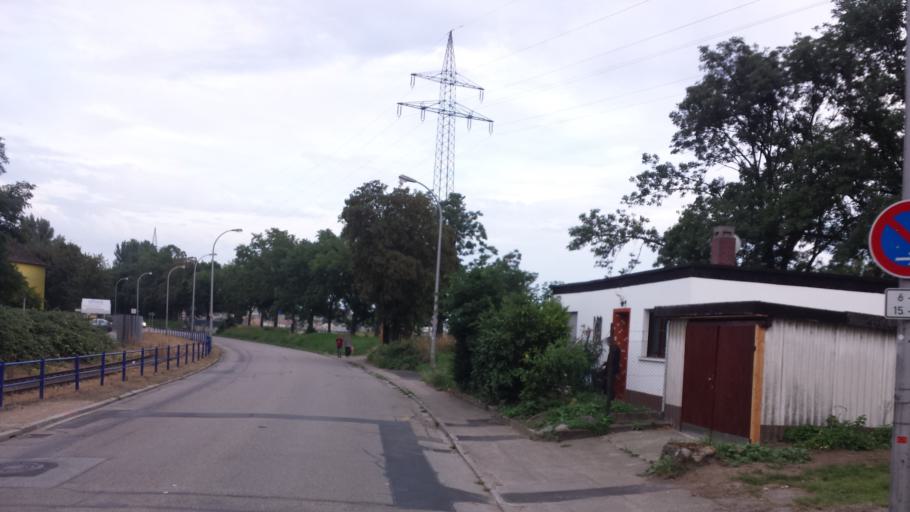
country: DE
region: Rheinland-Pfalz
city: Ludwigshafen am Rhein
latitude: 49.5059
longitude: 8.4486
